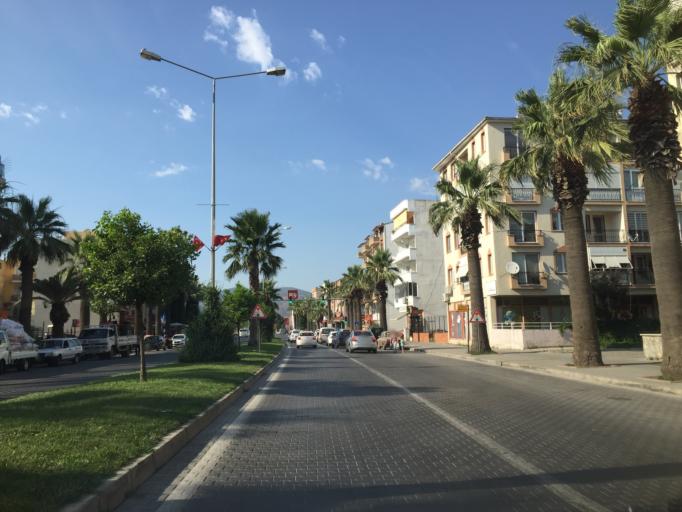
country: TR
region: Izmir
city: Selcuk
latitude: 37.9530
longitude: 27.3711
